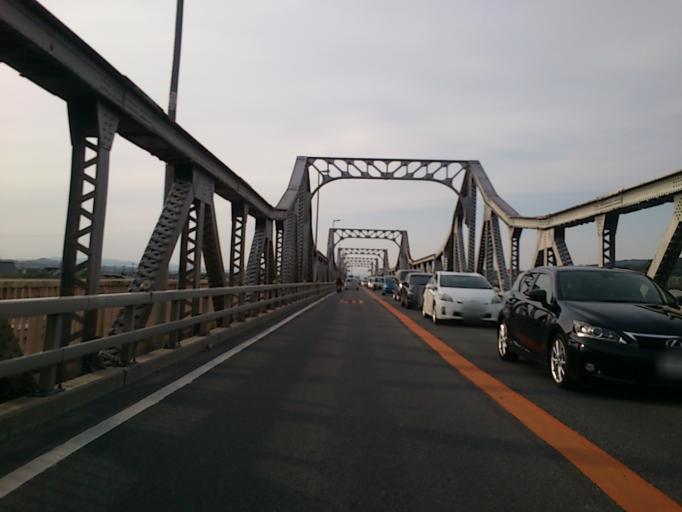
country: JP
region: Nara
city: Nara-shi
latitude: 34.7425
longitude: 135.8221
